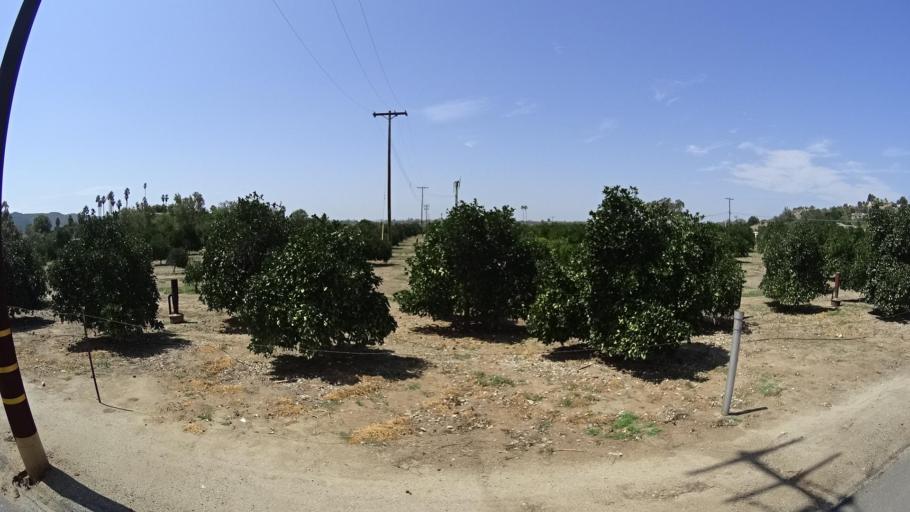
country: US
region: California
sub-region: San Diego County
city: Valley Center
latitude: 33.2351
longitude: -116.9936
